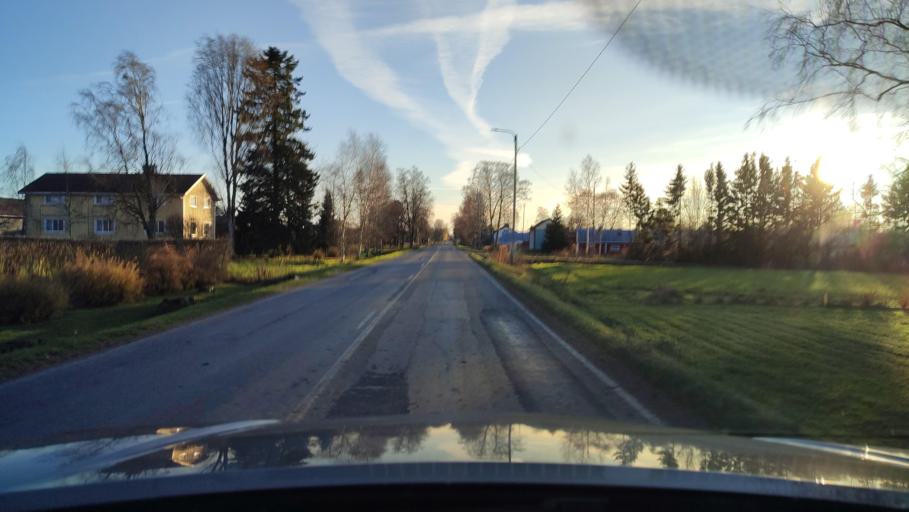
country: FI
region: Ostrobothnia
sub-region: Sydosterbotten
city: Naerpes
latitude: 62.6223
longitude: 21.4841
